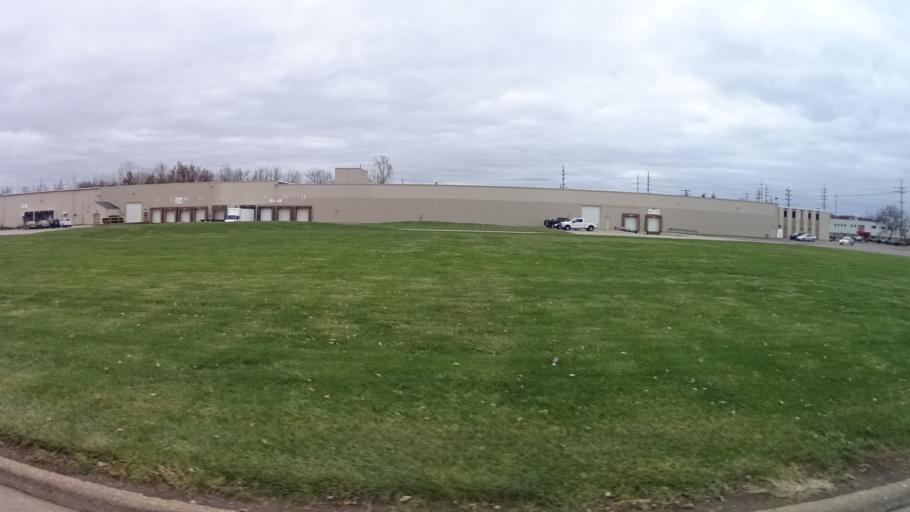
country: US
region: Ohio
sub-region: Lorain County
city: Avon Lake
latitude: 41.4813
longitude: -82.0457
